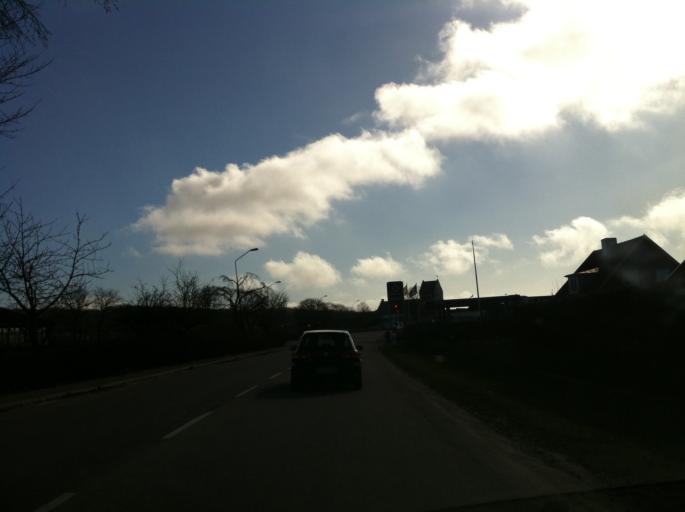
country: SE
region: Skane
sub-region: Bastads Kommun
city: Forslov
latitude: 56.3553
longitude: 12.8185
